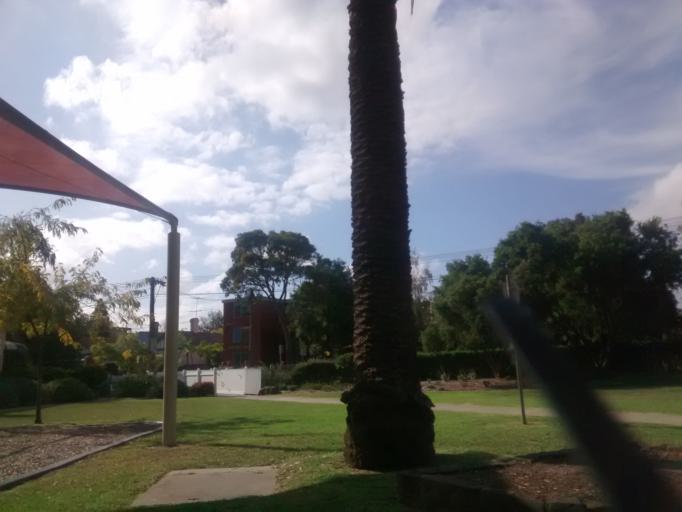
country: AU
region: Victoria
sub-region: Yarra
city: North Fitzroy
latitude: -37.7802
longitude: 144.9847
